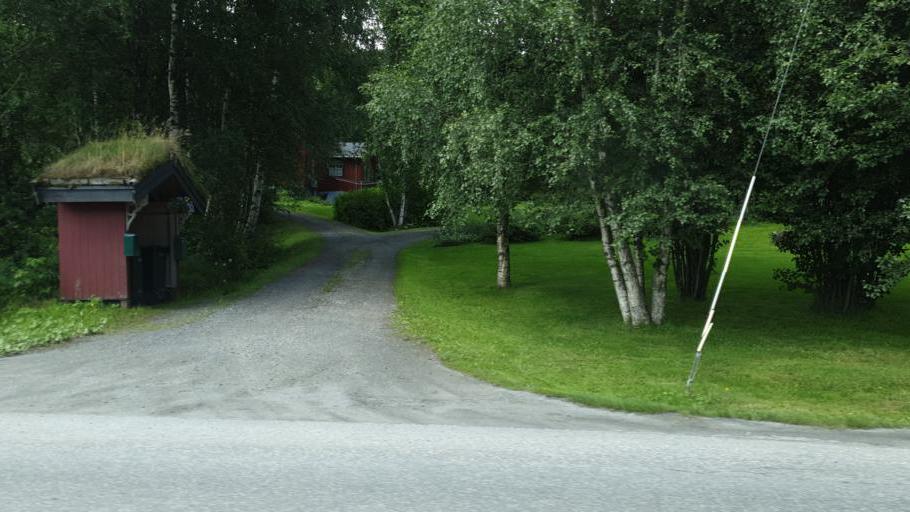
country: NO
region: Sor-Trondelag
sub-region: Midtre Gauldal
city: Storen
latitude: 62.9480
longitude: 10.1896
